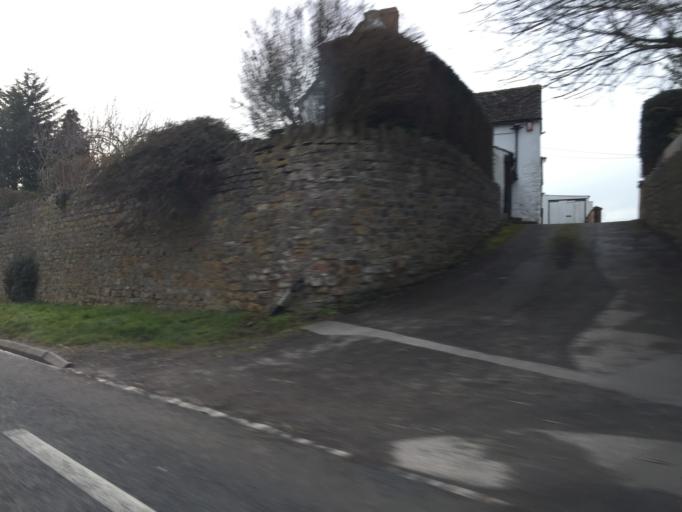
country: GB
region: England
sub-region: Gloucestershire
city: Dursley
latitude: 51.7103
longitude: -2.3862
